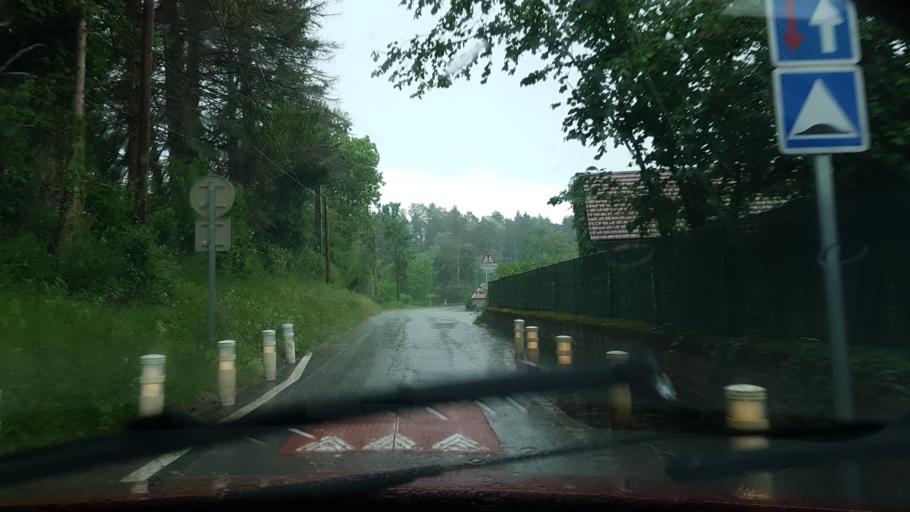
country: FR
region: Franche-Comte
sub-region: Departement du Jura
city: Clairvaux-les-Lacs
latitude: 46.5818
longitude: 5.7035
